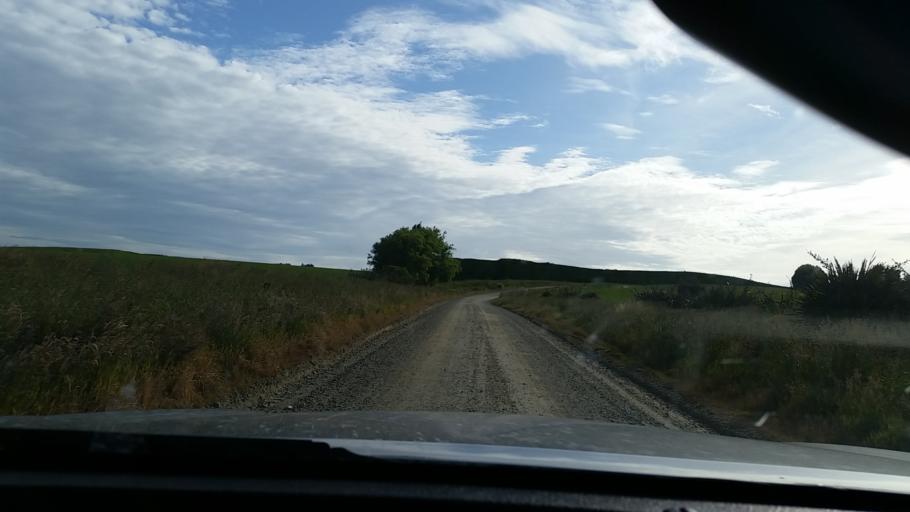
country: NZ
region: Southland
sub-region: Gore District
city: Gore
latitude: -46.2644
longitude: 168.7212
